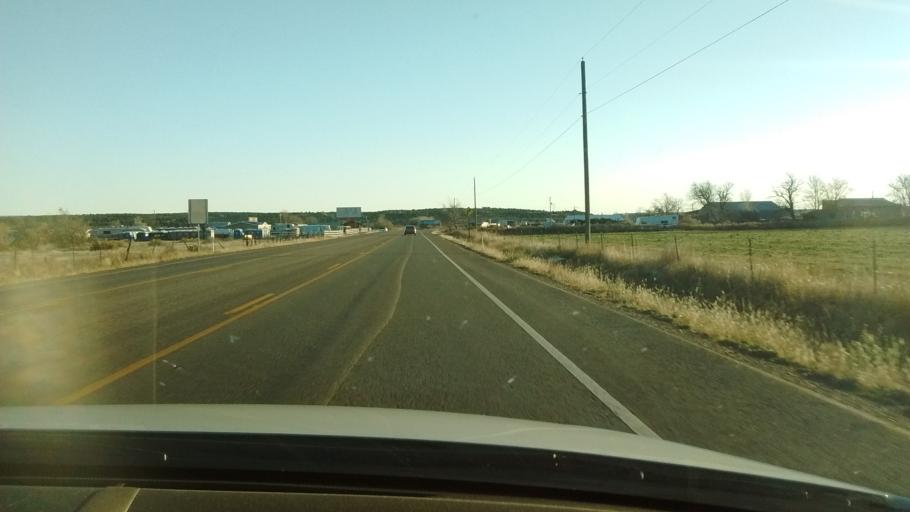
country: US
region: Utah
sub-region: Kane County
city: Kanab
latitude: 37.0162
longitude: -112.5250
